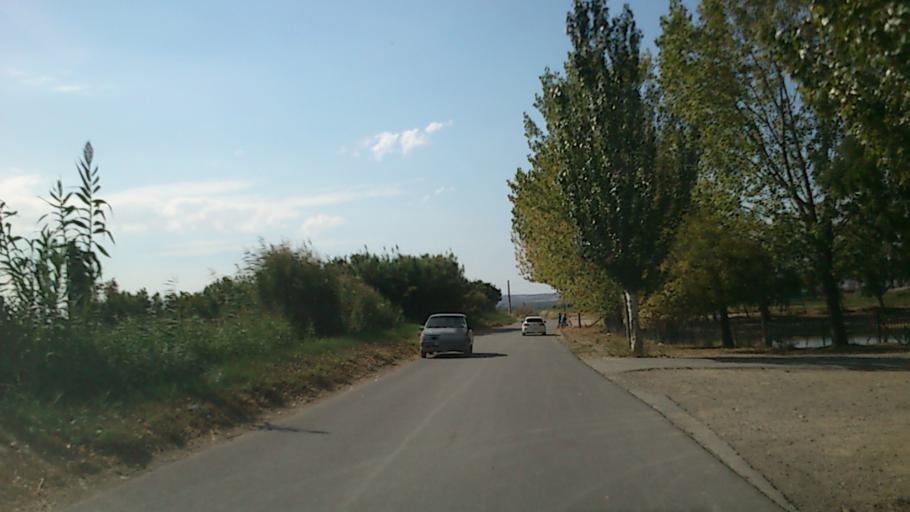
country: ES
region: Aragon
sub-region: Provincia de Zaragoza
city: Puebla de Alfinden
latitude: 41.6252
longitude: -0.7563
